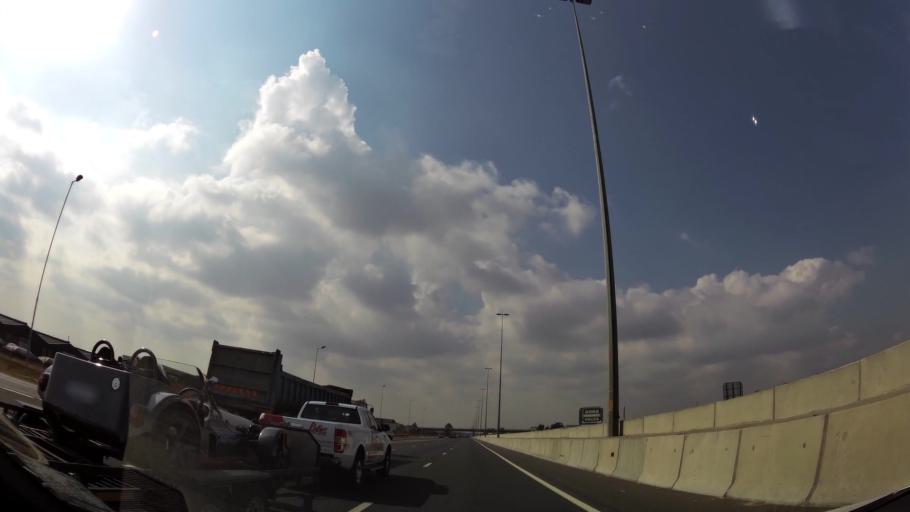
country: ZA
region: Gauteng
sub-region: Ekurhuleni Metropolitan Municipality
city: Boksburg
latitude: -26.1725
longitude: 28.2506
